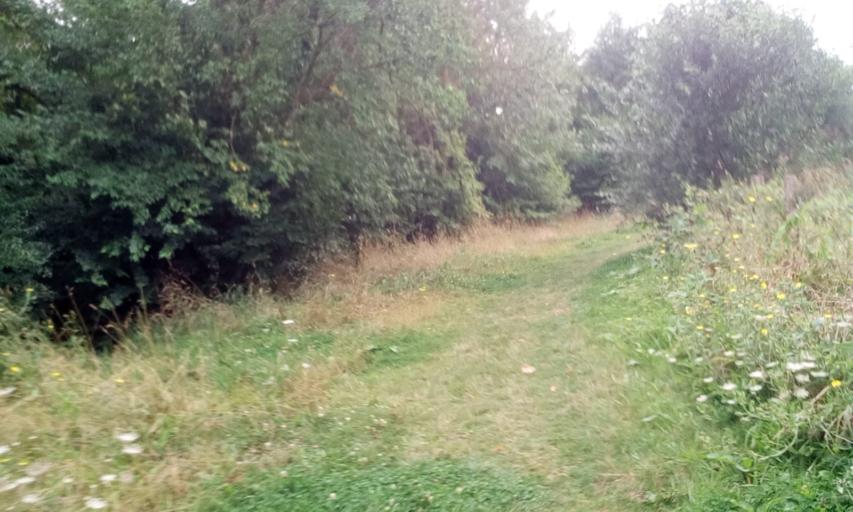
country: FR
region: Lower Normandy
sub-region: Departement du Calvados
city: Verson
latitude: 49.1510
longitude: -0.4524
